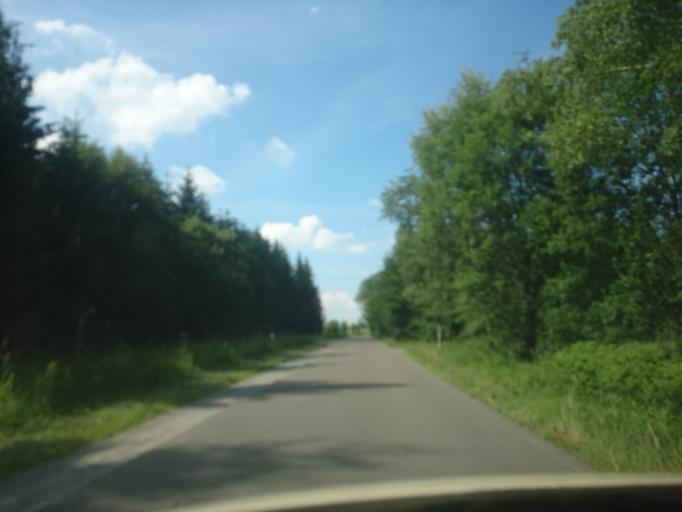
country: DE
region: Saxony
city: Eppendorf
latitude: 50.7781
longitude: 13.2245
